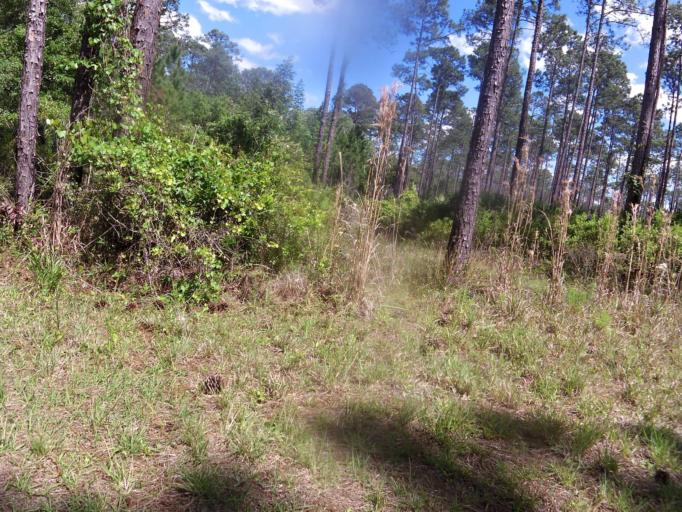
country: US
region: Florida
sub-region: Clay County
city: Green Cove Springs
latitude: 29.9629
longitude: -81.6314
